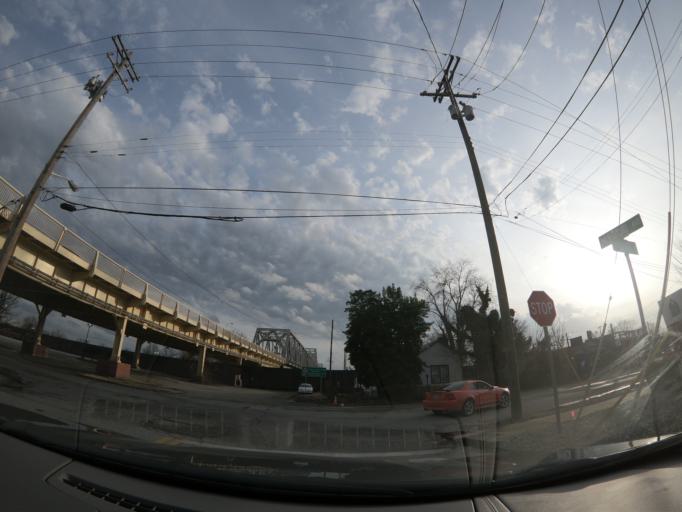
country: US
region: Indiana
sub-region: Clark County
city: Jeffersonville
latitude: 38.2698
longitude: -85.7505
